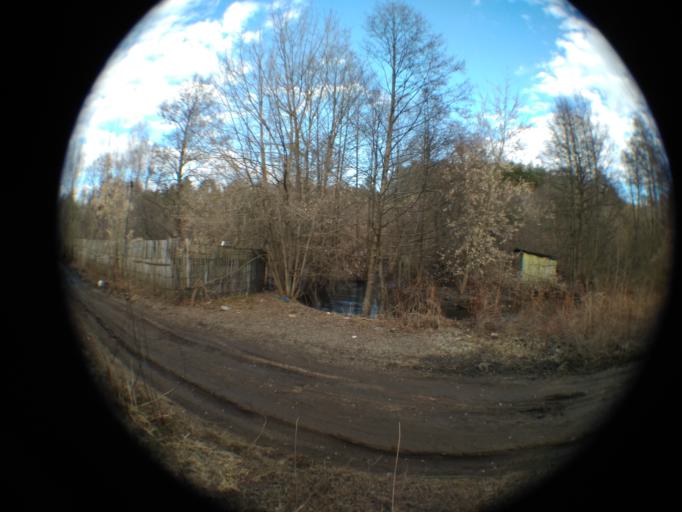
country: RU
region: Moskovskaya
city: Kratovo
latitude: 55.5708
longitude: 38.1700
